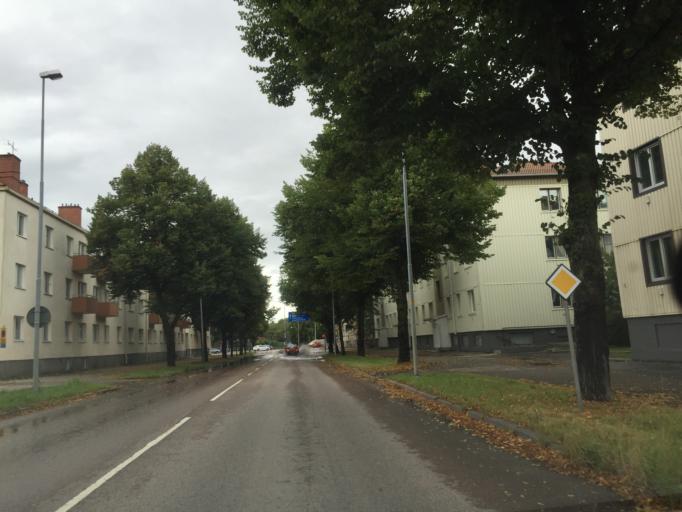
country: SE
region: Soedermanland
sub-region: Eskilstuna Kommun
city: Eskilstuna
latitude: 59.3658
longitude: 16.5289
